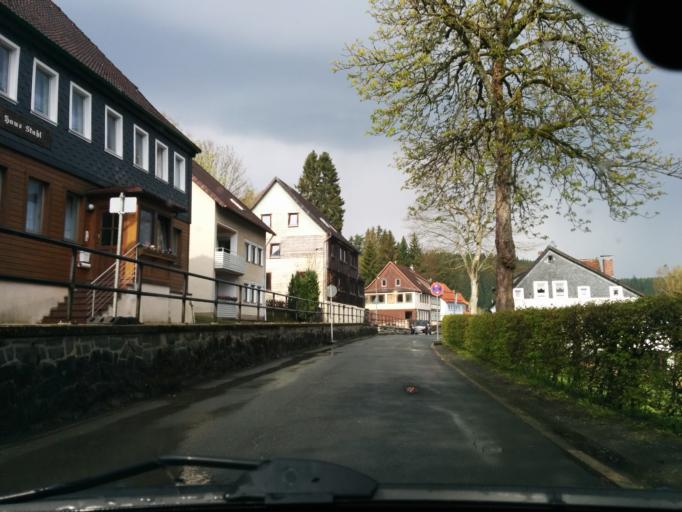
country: DE
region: Lower Saxony
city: Altenau
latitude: 51.8032
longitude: 10.4423
